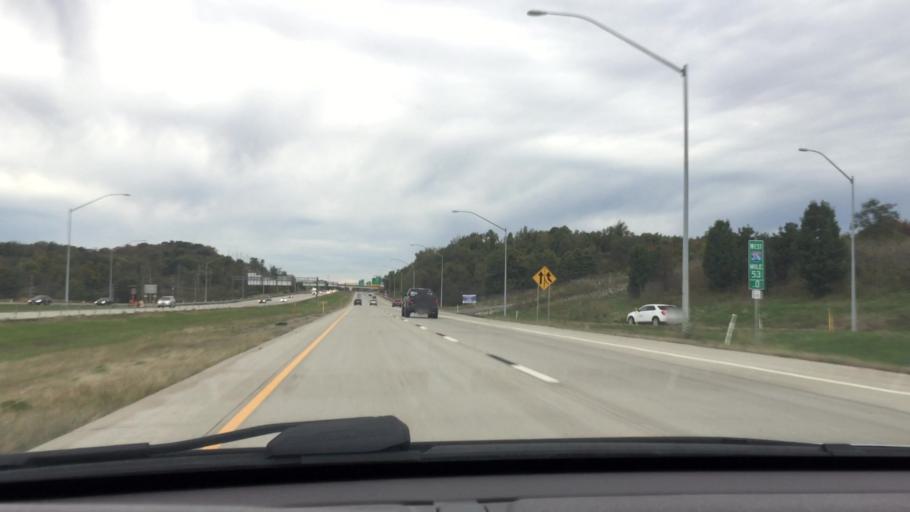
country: US
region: Pennsylvania
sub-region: Allegheny County
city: Imperial
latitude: 40.4907
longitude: -80.2713
